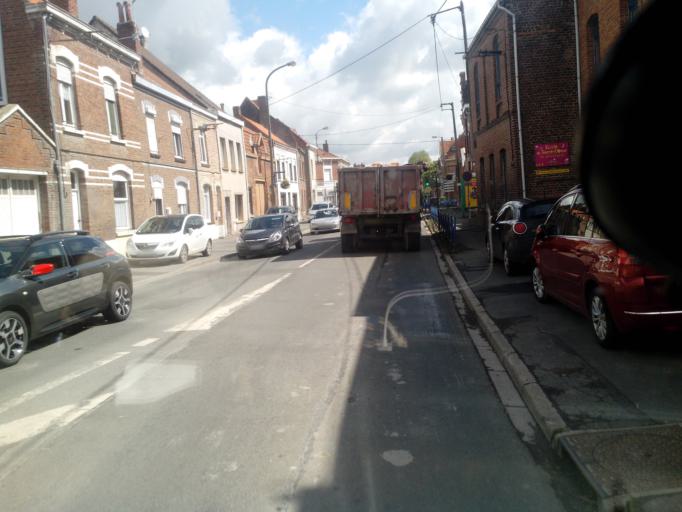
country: FR
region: Nord-Pas-de-Calais
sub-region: Departement du Pas-de-Calais
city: Sailly-sur-la-Lys
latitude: 50.6571
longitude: 2.7681
